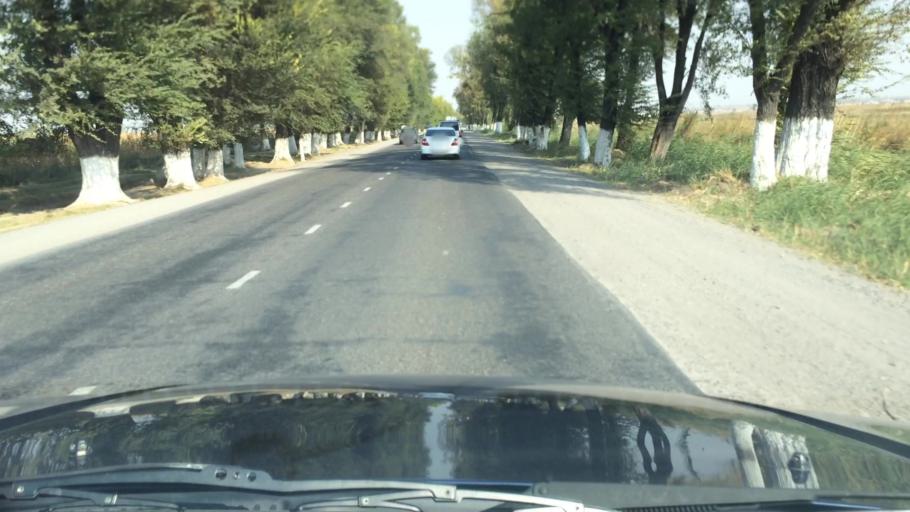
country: KG
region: Chuy
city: Lebedinovka
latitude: 42.9021
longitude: 74.6855
